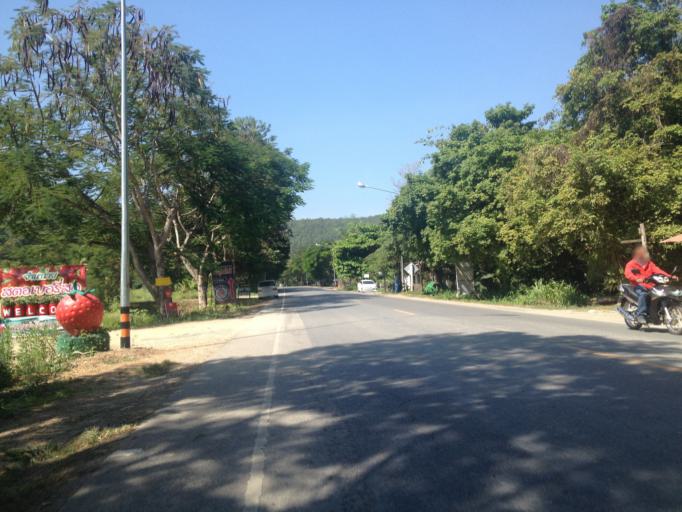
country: TH
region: Chiang Mai
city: Hang Dong
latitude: 18.7353
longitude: 98.9037
